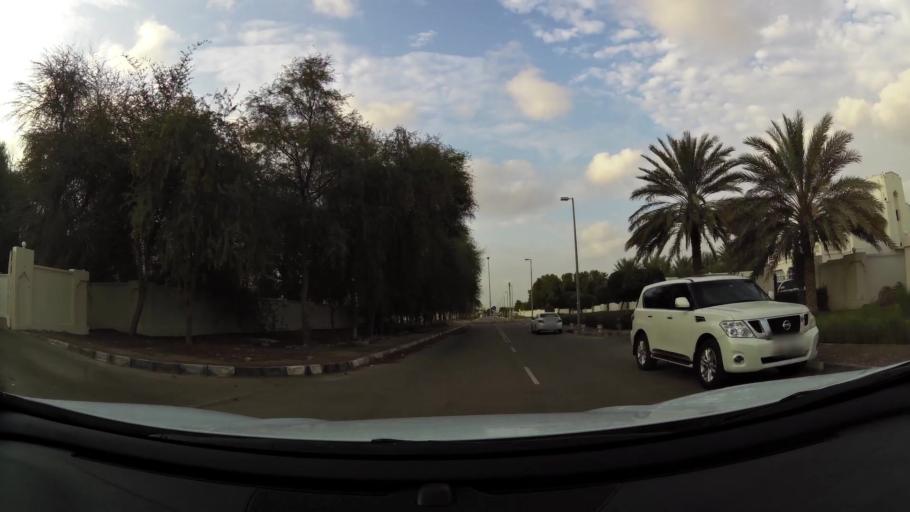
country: AE
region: Abu Dhabi
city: Abu Dhabi
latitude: 24.3823
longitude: 54.5326
